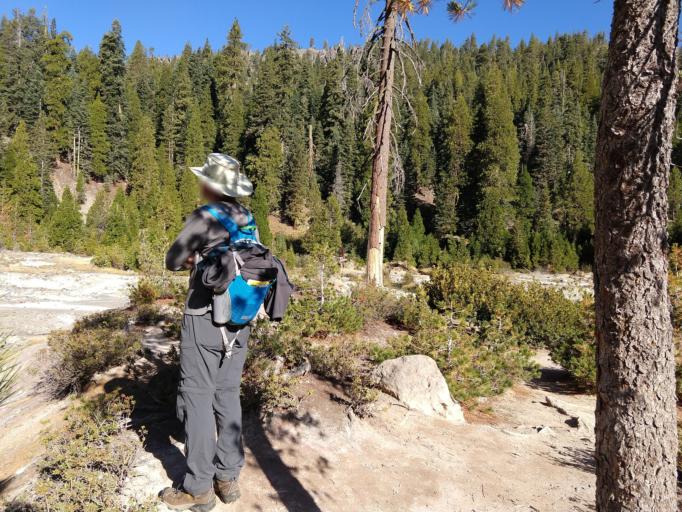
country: US
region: California
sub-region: Plumas County
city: Chester
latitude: 40.4415
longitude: -121.4344
